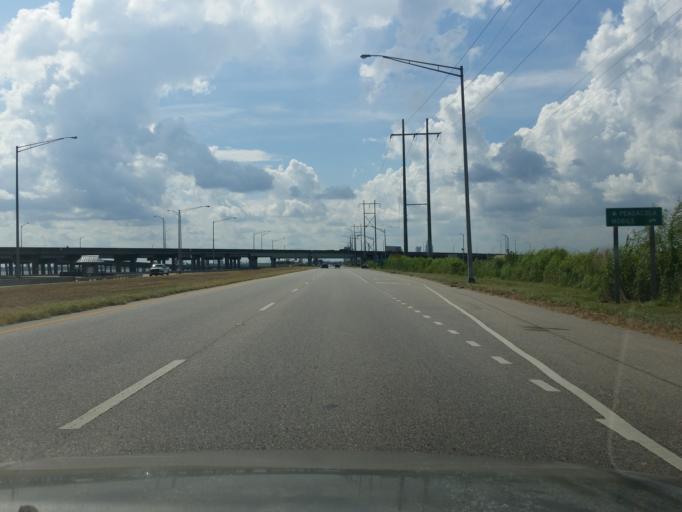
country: US
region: Alabama
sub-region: Mobile County
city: Mobile
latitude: 30.6775
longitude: -87.9829
